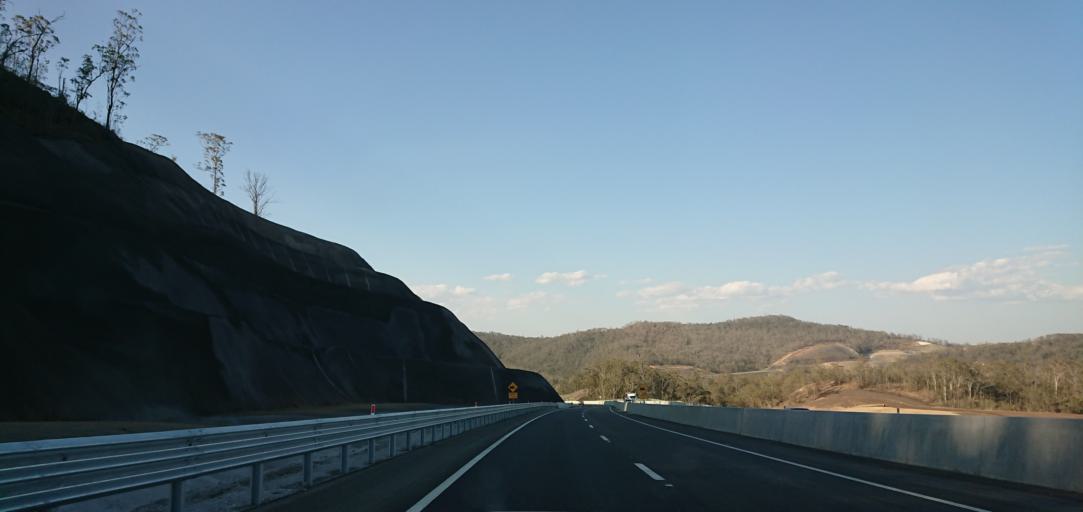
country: AU
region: Queensland
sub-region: Toowoomba
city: Wilsonton Heights
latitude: -27.5084
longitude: 151.9688
